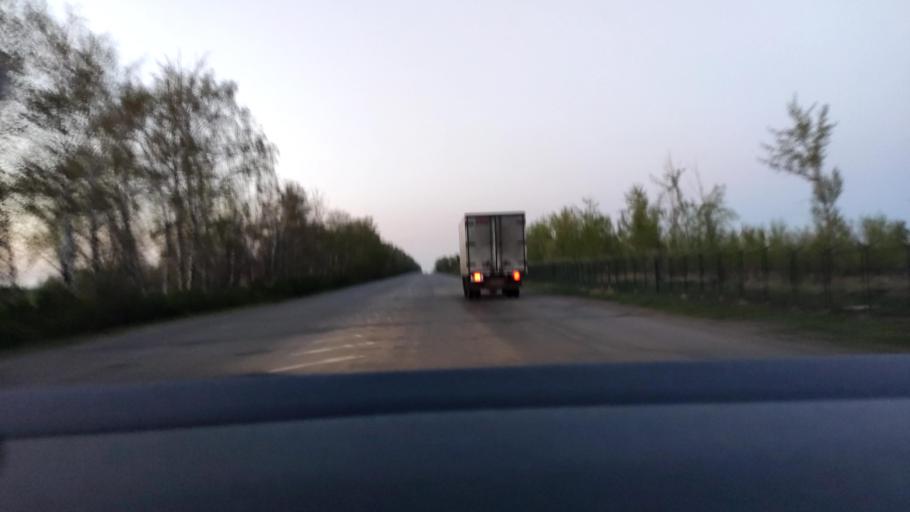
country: RU
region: Voronezj
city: Maslovka
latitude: 51.5255
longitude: 39.2958
